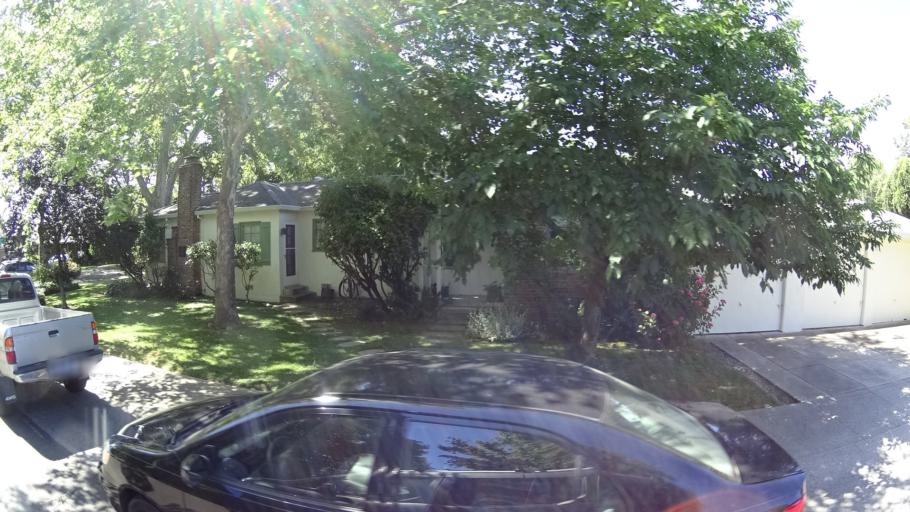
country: US
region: California
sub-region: Sacramento County
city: Sacramento
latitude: 38.5503
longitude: -121.4970
